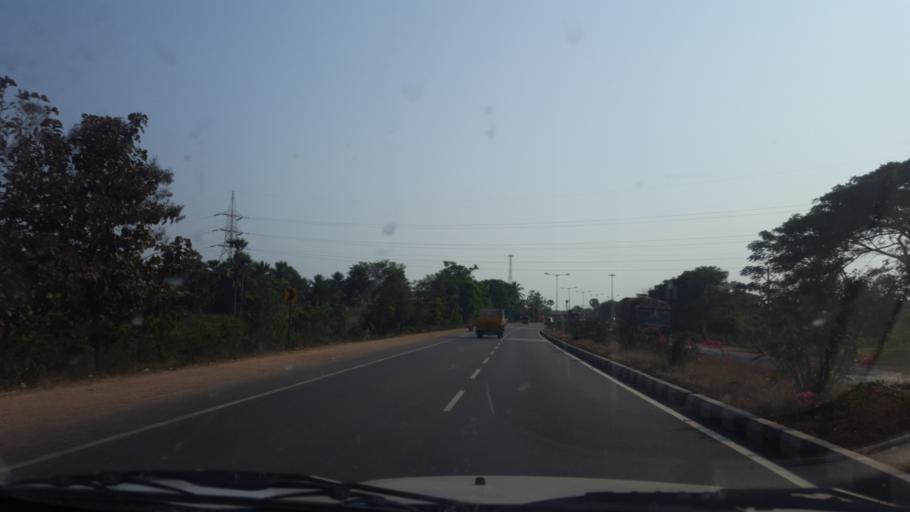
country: IN
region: Andhra Pradesh
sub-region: Vishakhapatnam
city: Elamanchili
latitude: 17.5674
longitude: 82.8616
